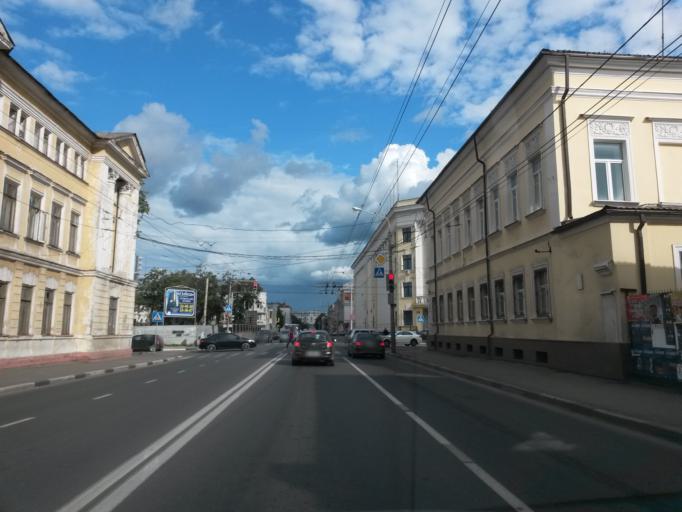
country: RU
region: Jaroslavl
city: Yaroslavl
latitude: 57.6333
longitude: 39.8796
